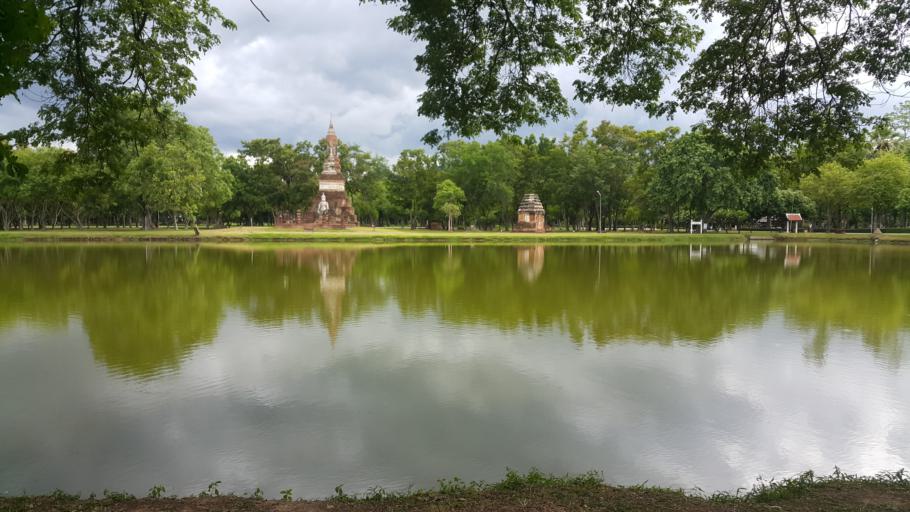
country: TH
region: Sukhothai
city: Ban Na
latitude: 17.0168
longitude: 99.7011
